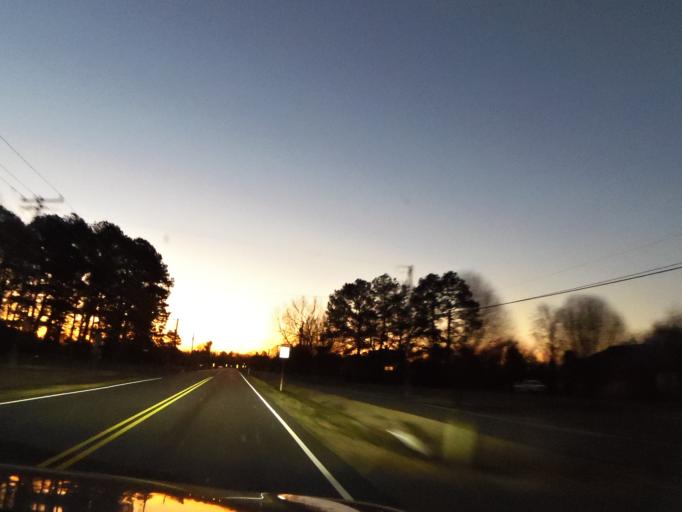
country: US
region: Virginia
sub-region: Henrico County
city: Montrose
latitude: 37.4876
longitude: -77.4008
